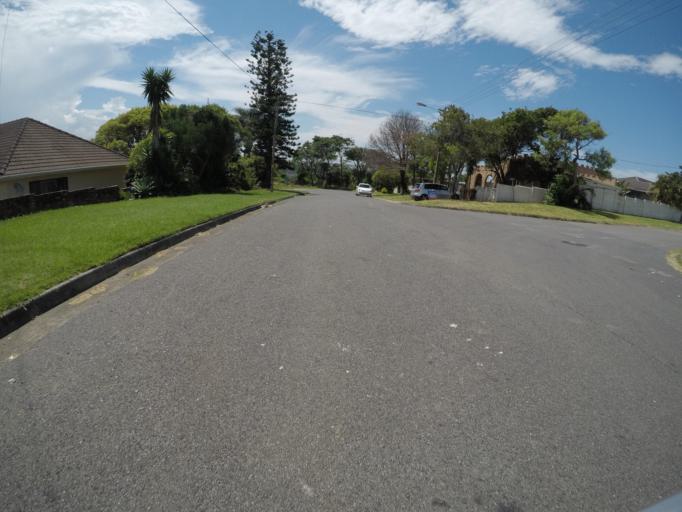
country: ZA
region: Eastern Cape
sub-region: Buffalo City Metropolitan Municipality
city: East London
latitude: -33.0299
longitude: 27.8705
